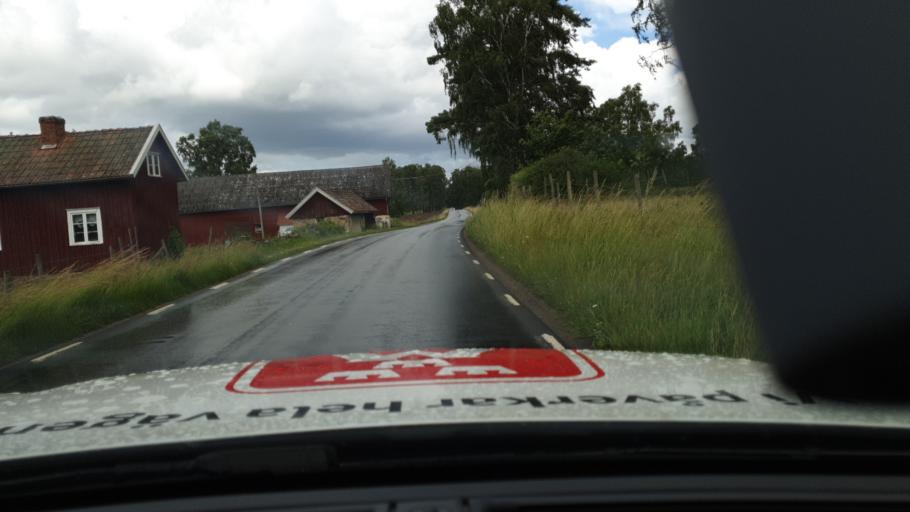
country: SE
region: Vaestra Goetaland
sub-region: Falkopings Kommun
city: Akarp
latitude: 58.2668
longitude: 13.5979
